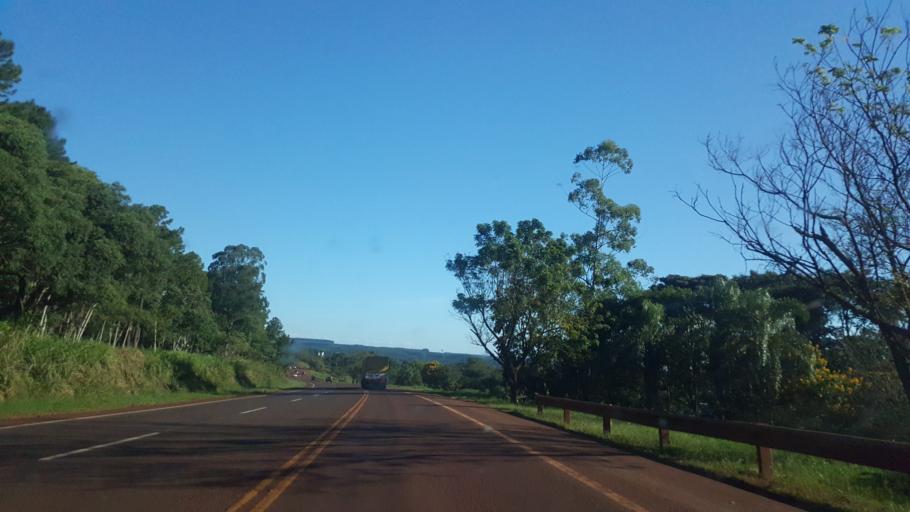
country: AR
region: Misiones
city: Puerto Esperanza
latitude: -26.1805
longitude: -54.5895
